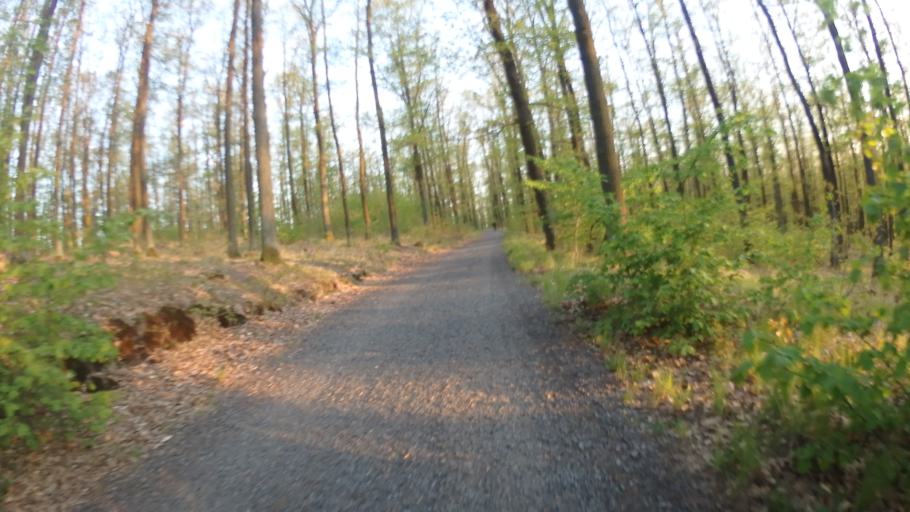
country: CZ
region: South Moravian
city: Troubsko
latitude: 49.1904
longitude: 16.5161
